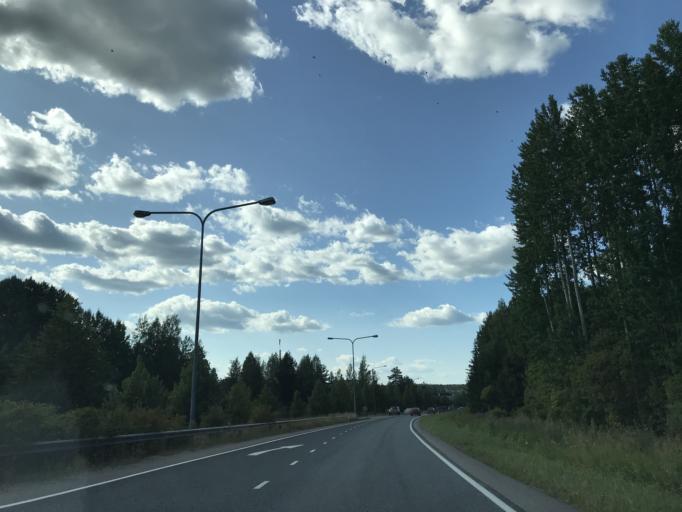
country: FI
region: Uusimaa
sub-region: Helsinki
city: Nurmijaervi
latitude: 60.4595
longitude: 24.8176
